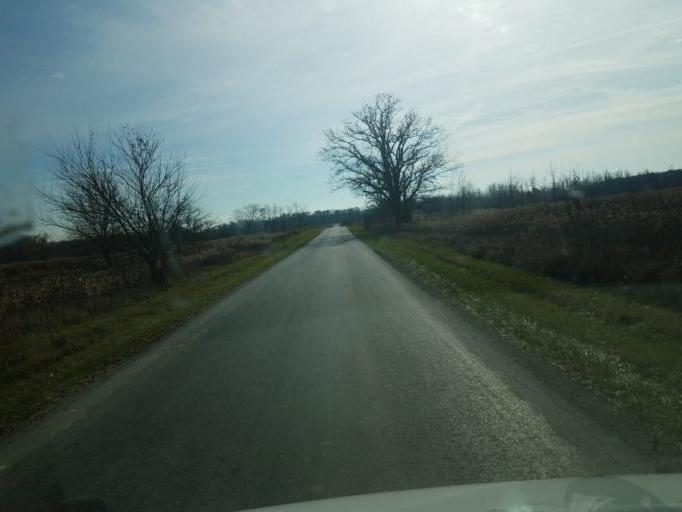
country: US
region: Ohio
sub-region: Hardin County
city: Kenton
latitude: 40.6171
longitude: -83.4386
